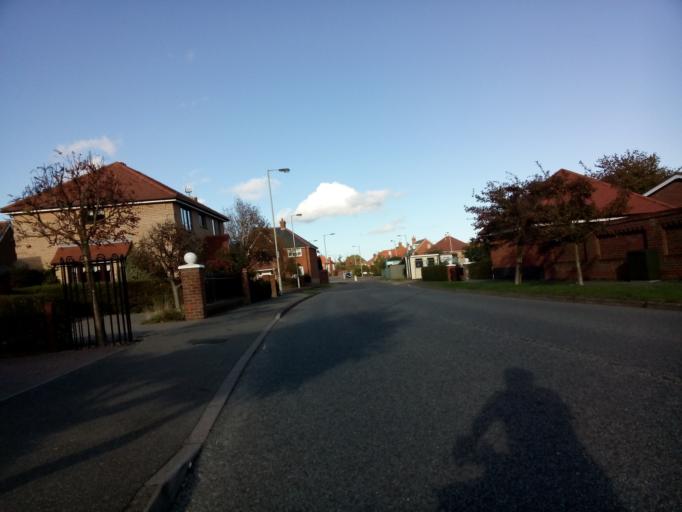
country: GB
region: England
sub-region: Suffolk
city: Kesgrave
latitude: 52.0530
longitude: 1.2146
